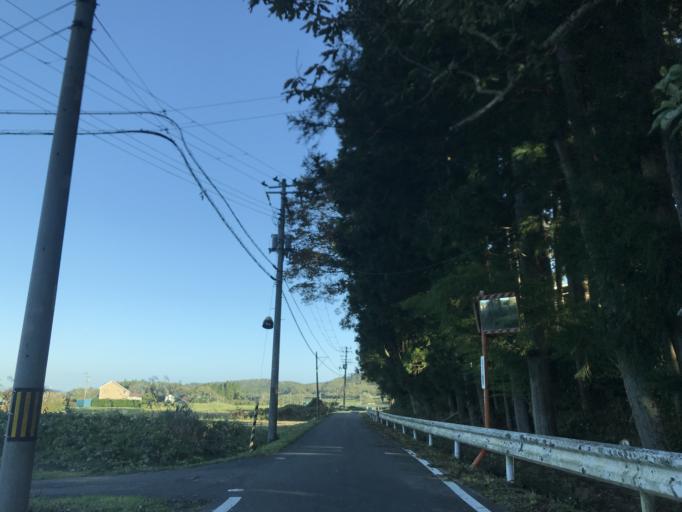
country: JP
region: Iwate
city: Ichinoseki
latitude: 38.9416
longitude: 141.0476
